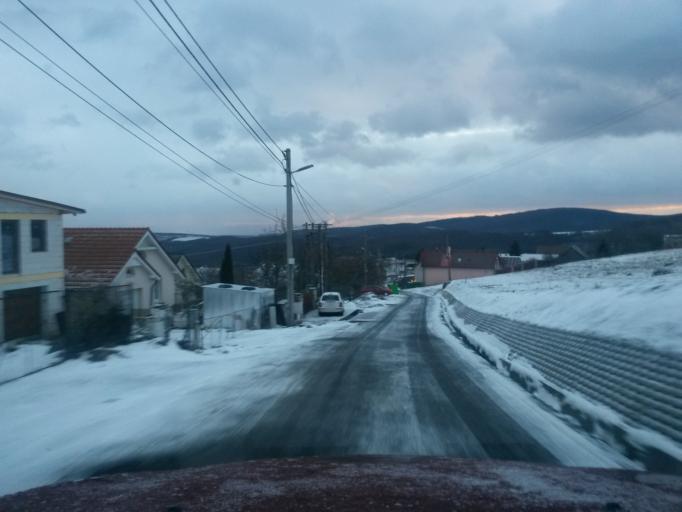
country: SK
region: Kosicky
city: Kosice
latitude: 48.7445
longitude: 21.1223
